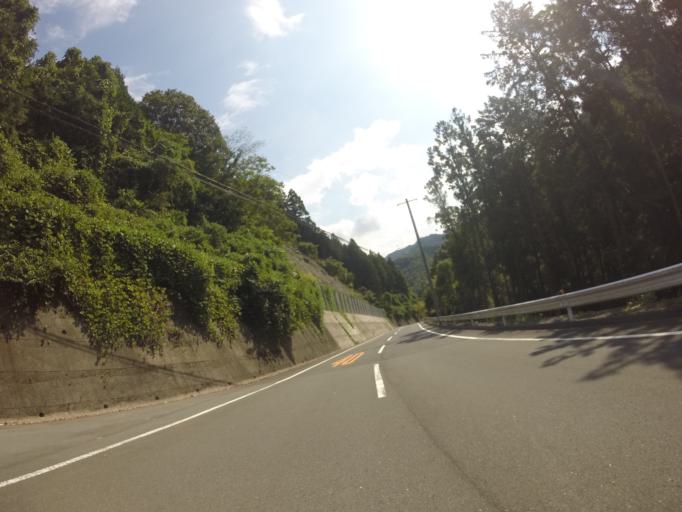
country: JP
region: Shizuoka
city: Shizuoka-shi
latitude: 35.1071
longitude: 138.4716
